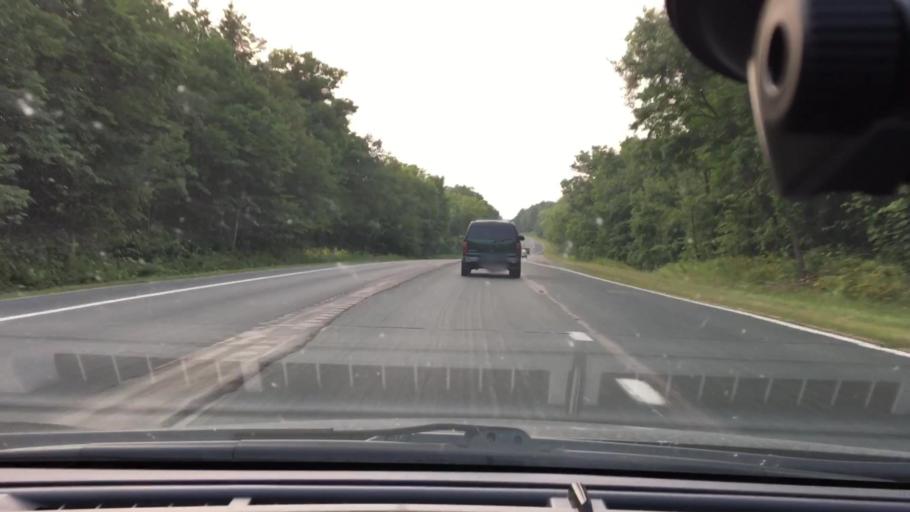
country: US
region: Minnesota
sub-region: Mille Lacs County
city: Vineland
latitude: 46.2359
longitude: -93.7999
